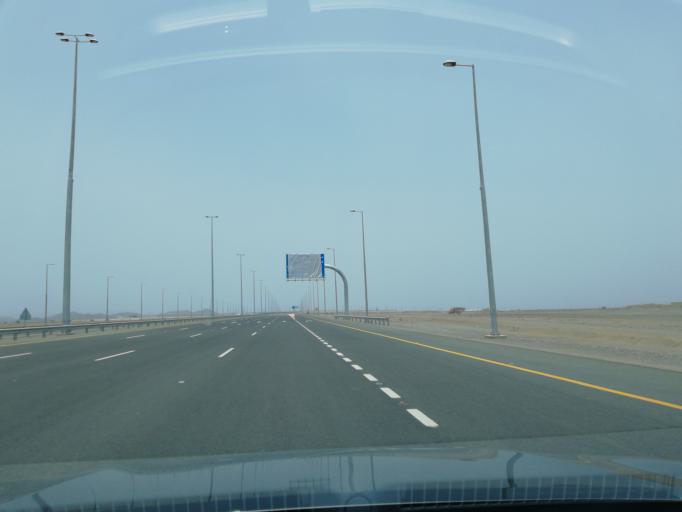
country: OM
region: Al Batinah
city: Al Liwa'
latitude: 24.4426
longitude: 56.5213
